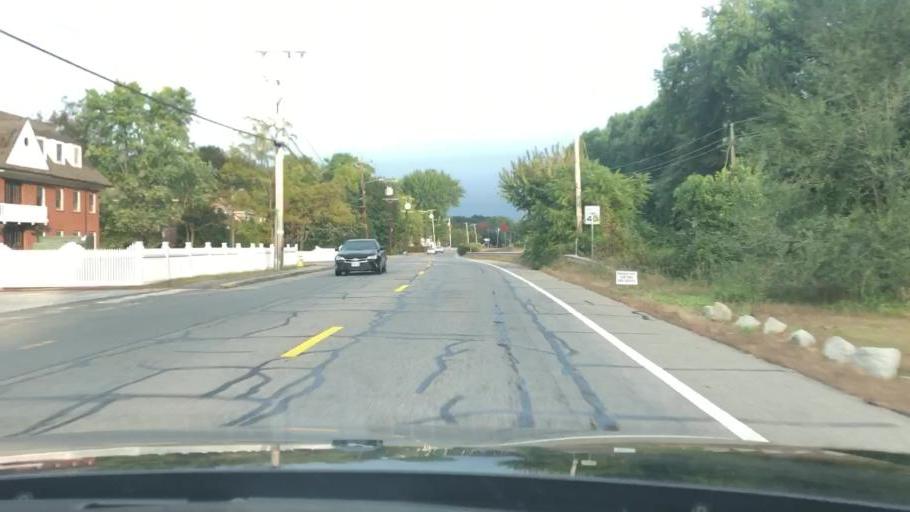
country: US
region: Massachusetts
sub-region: Middlesex County
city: Tyngsboro
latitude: 42.6458
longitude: -71.3934
